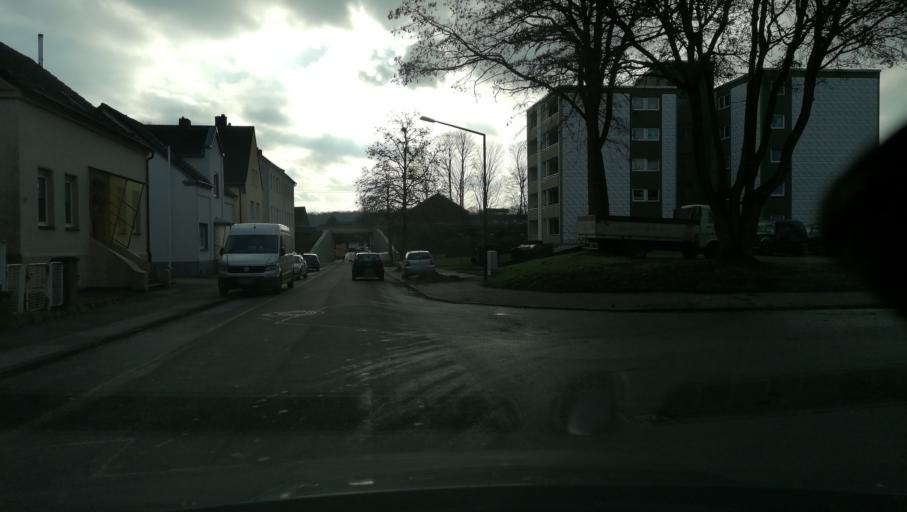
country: DE
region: North Rhine-Westphalia
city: Herten
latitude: 51.6010
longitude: 7.1575
